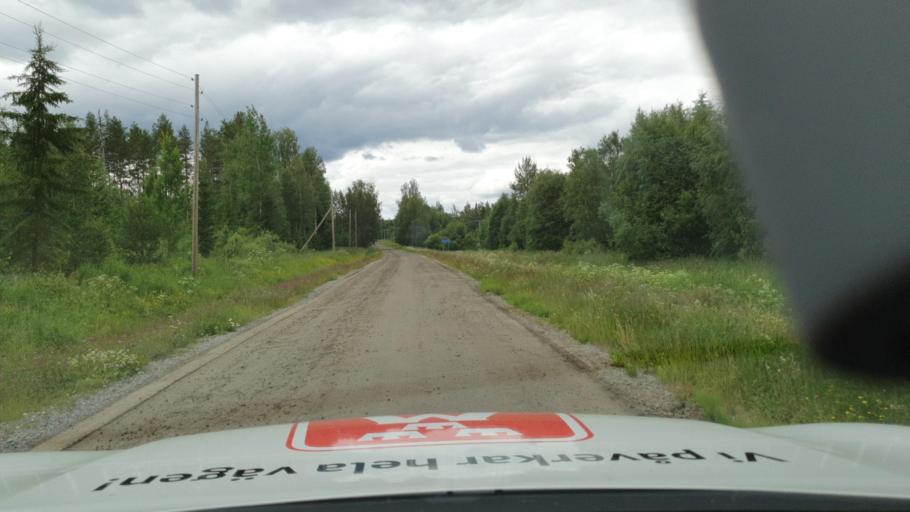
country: SE
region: Vaesterbotten
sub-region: Bjurholms Kommun
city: Bjurholm
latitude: 63.8012
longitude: 19.0831
